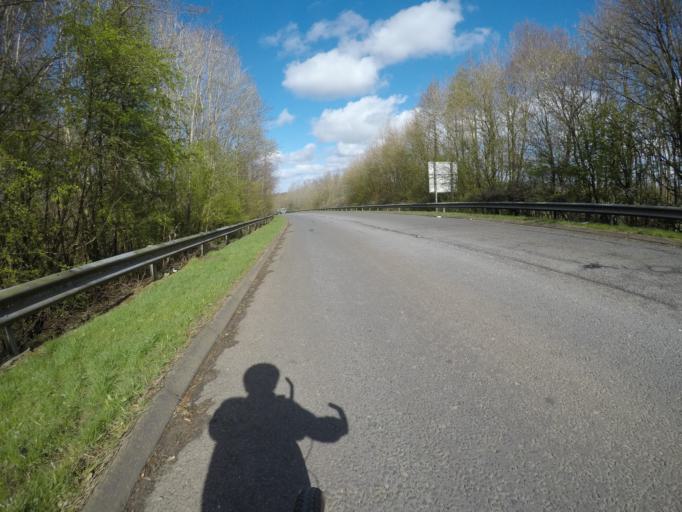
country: GB
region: Scotland
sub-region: North Ayrshire
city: Springside
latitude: 55.6130
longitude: -4.6040
